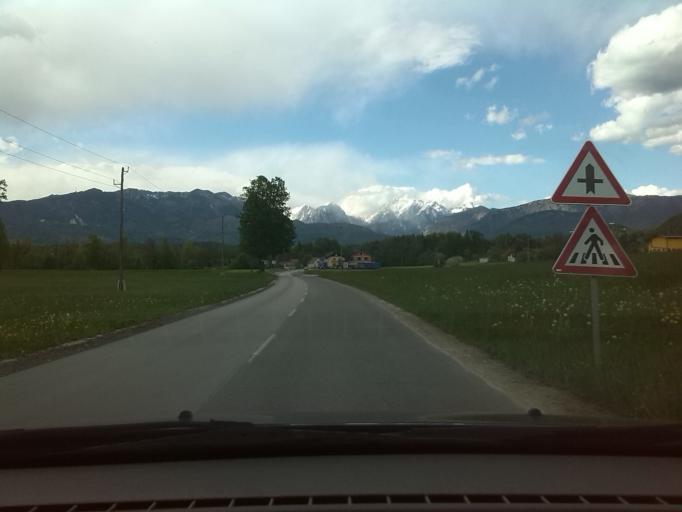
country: SI
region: Kamnik
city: Smarca
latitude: 46.1931
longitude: 14.6020
